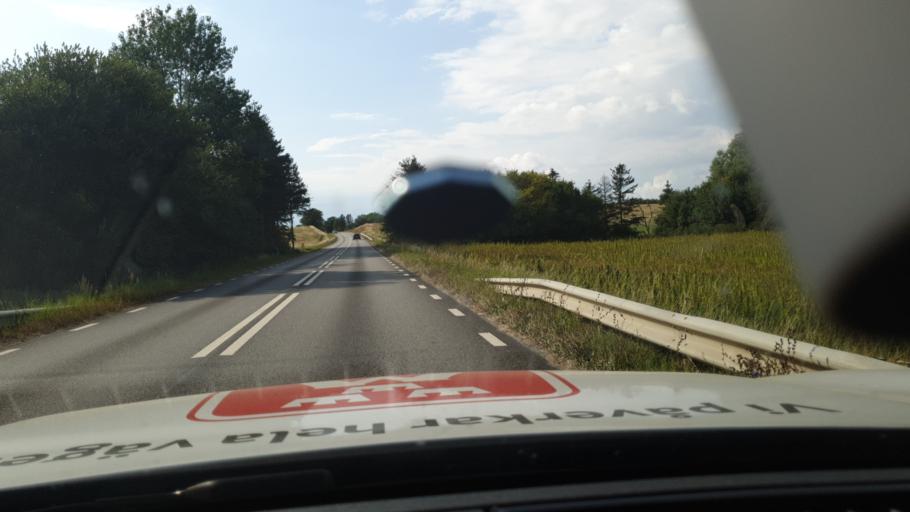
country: SE
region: Skane
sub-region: Svedala Kommun
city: Svedala
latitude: 55.4524
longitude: 13.2389
